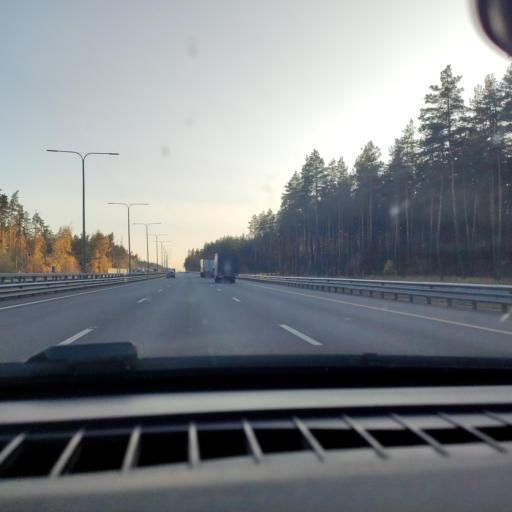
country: RU
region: Voronezj
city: Somovo
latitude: 51.7164
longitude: 39.3075
